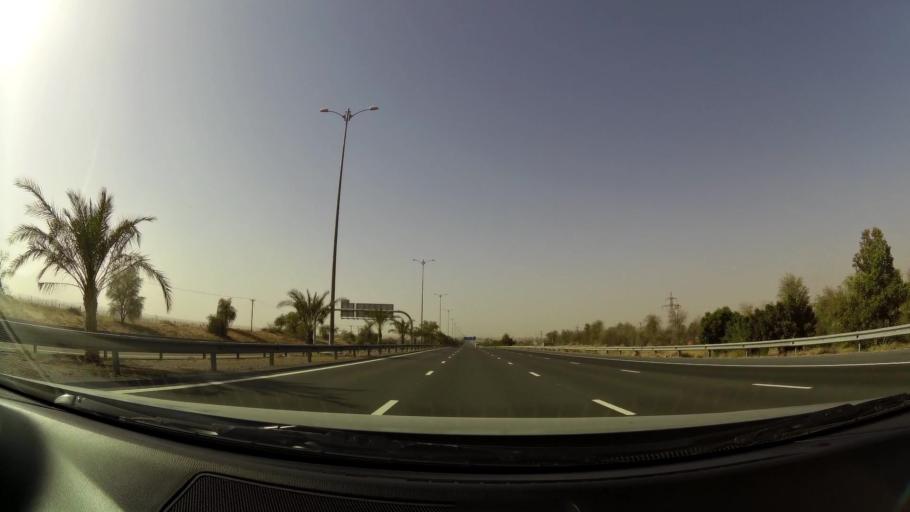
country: OM
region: Al Buraimi
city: Al Buraymi
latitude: 24.5363
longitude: 55.7580
